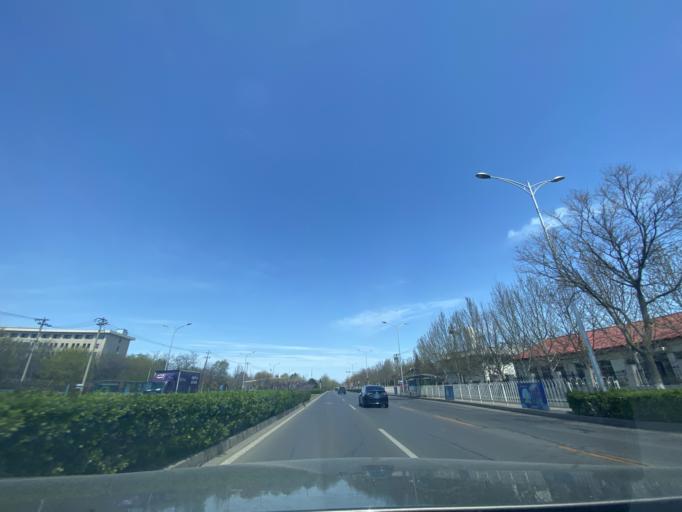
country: CN
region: Beijing
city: Sijiqing
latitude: 39.9411
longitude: 116.2405
